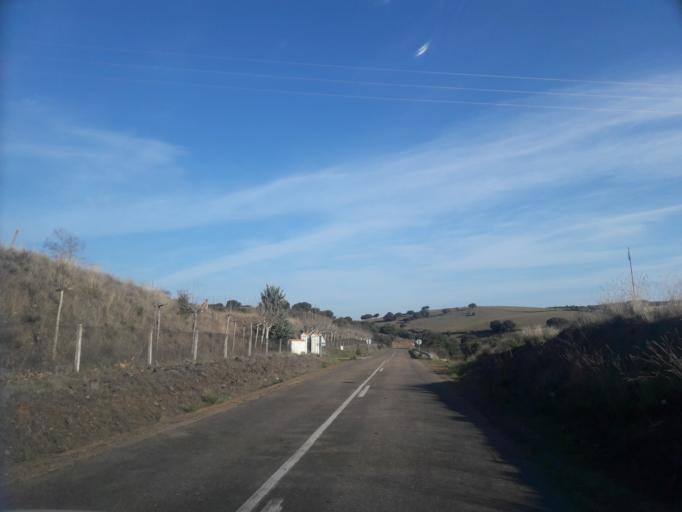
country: ES
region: Castille and Leon
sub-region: Provincia de Salamanca
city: Salvatierra de Tormes
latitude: 40.5889
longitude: -5.6044
